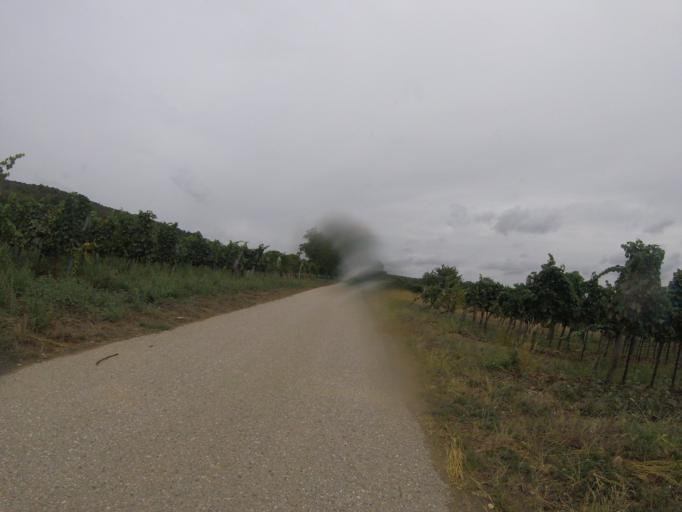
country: AT
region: Burgenland
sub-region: Politischer Bezirk Neusiedl am See
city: Jois
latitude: 47.9740
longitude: 16.7763
